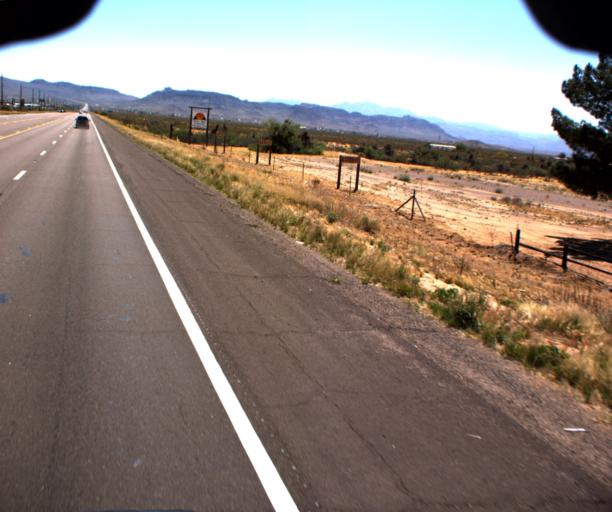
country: US
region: Arizona
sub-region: Mohave County
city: Golden Valley
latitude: 35.2220
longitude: -114.2181
